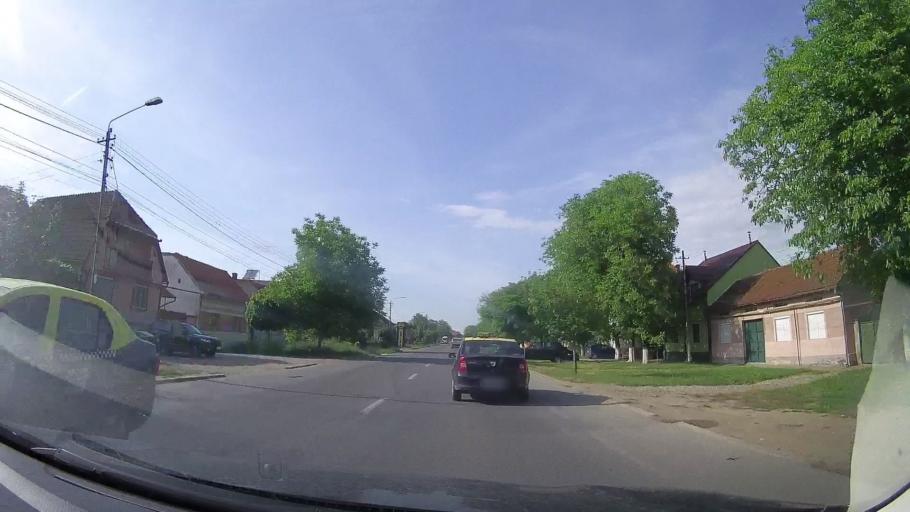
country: RO
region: Caras-Severin
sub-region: Municipiul Caransebes
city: Caransebes
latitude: 45.3987
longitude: 22.2252
